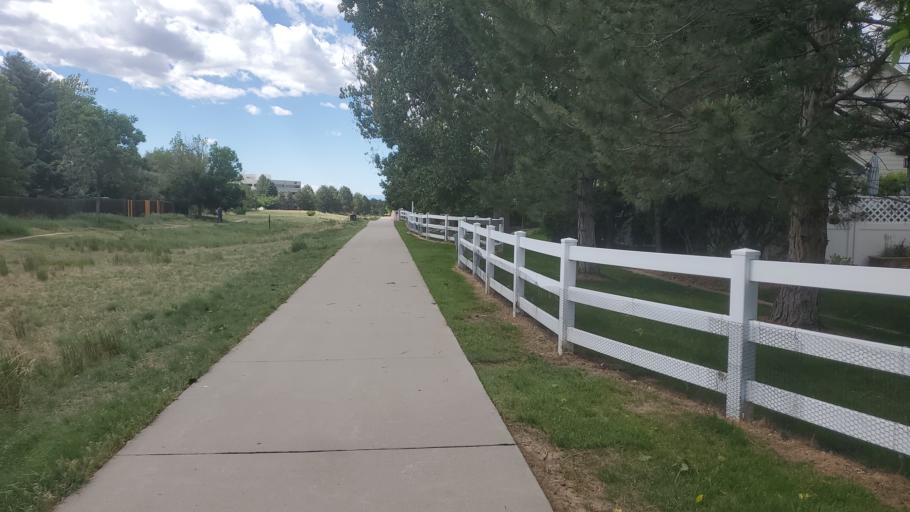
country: US
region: Colorado
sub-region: Adams County
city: Aurora
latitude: 39.6707
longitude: -104.8420
